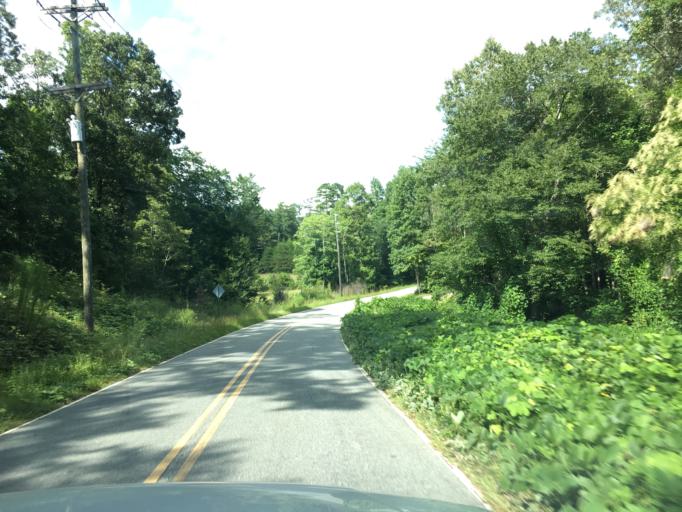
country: US
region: North Carolina
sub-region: Rutherford County
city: Lake Lure
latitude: 35.3909
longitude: -82.1924
